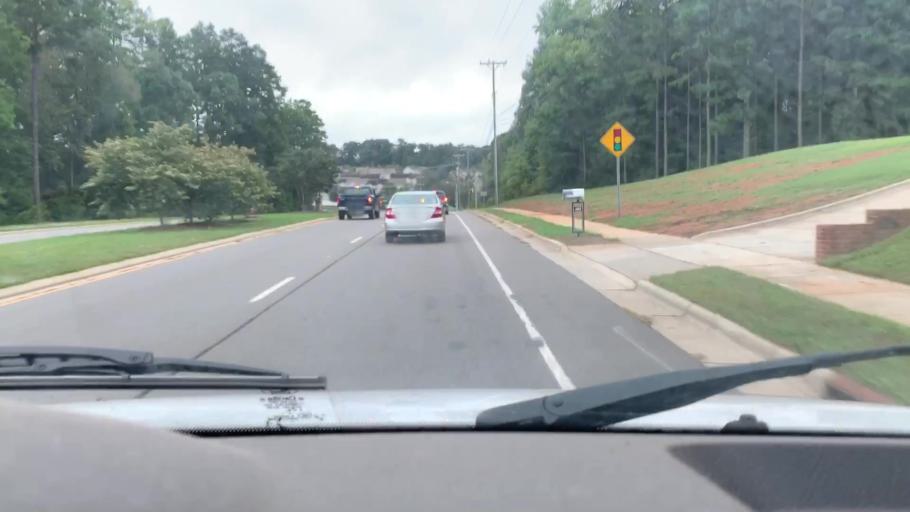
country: US
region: North Carolina
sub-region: Iredell County
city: Mooresville
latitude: 35.5818
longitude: -80.8635
